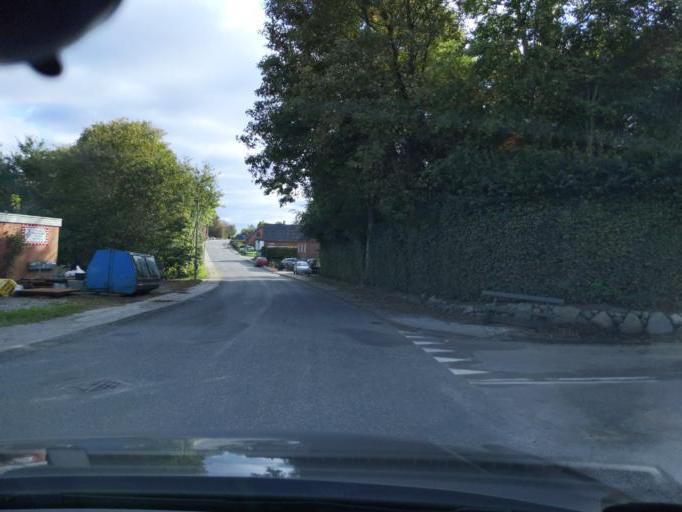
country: DK
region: North Denmark
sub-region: Mariagerfjord Kommune
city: Hobro
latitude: 56.5298
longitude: 9.7262
